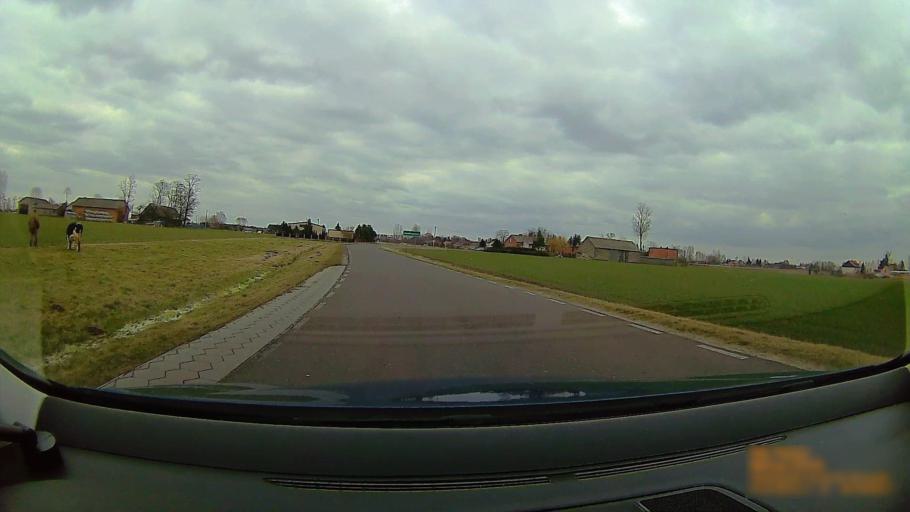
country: PL
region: Greater Poland Voivodeship
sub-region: Powiat koninski
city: Rzgow Pierwszy
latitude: 52.1064
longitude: 18.0833
